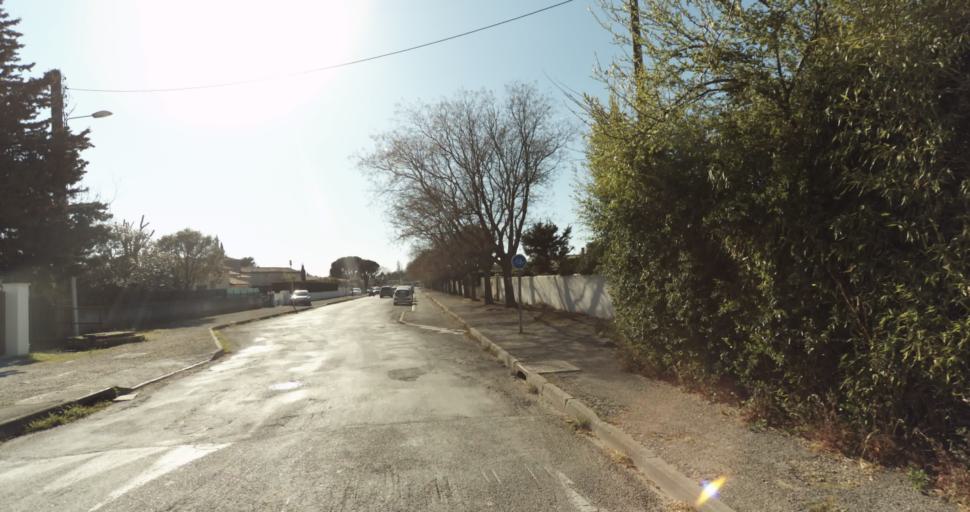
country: FR
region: Provence-Alpes-Cote d'Azur
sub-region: Departement des Bouches-du-Rhone
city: Pelissanne
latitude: 43.6339
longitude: 5.1437
